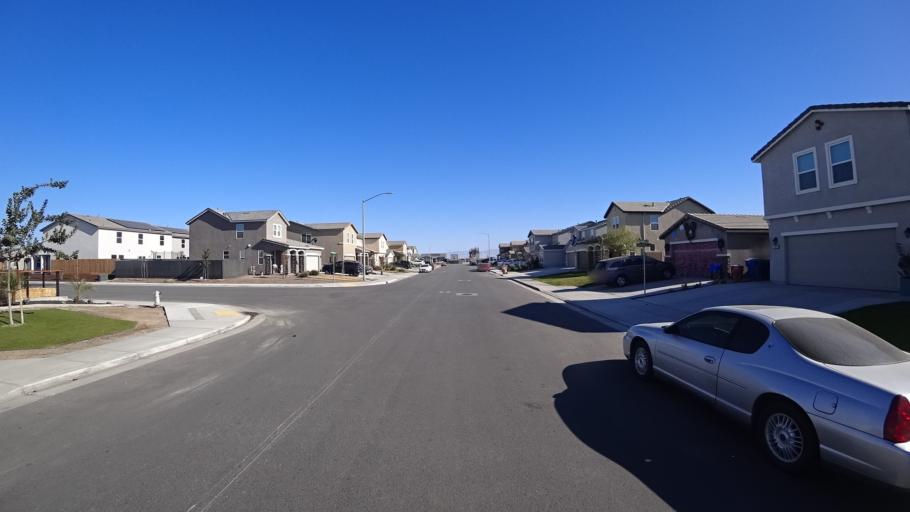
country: US
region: California
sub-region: Kern County
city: Greenfield
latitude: 35.2645
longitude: -119.0680
